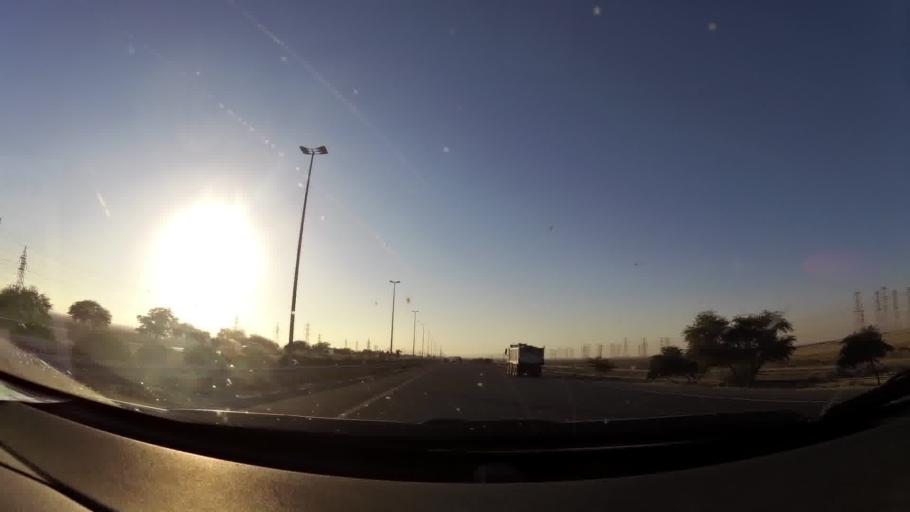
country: KW
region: Al Ahmadi
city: Al Fahahil
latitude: 28.8619
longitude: 48.2385
